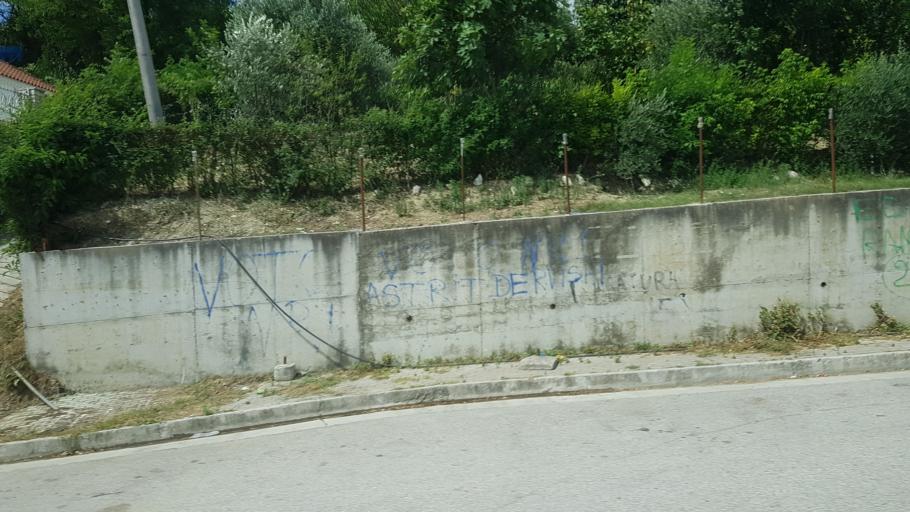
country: AL
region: Gjirokaster
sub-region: Rrethi i Tepelenes
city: Krahes
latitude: 40.4314
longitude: 19.8526
